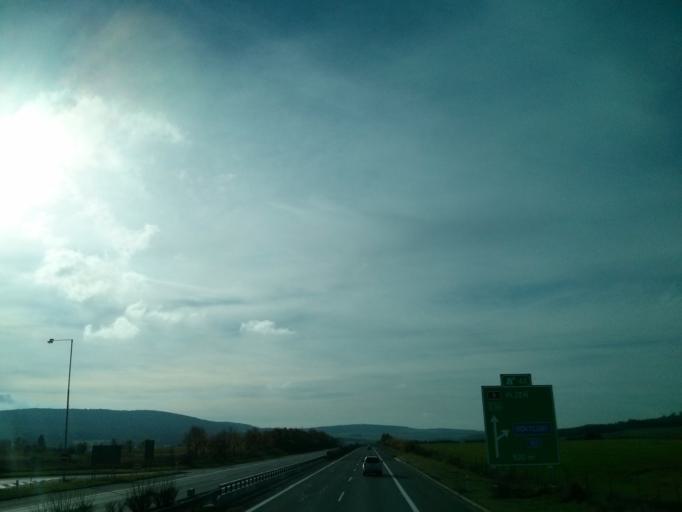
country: CZ
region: Plzensky
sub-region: Okres Rokycany
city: Rokycany
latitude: 49.7539
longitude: 13.5881
